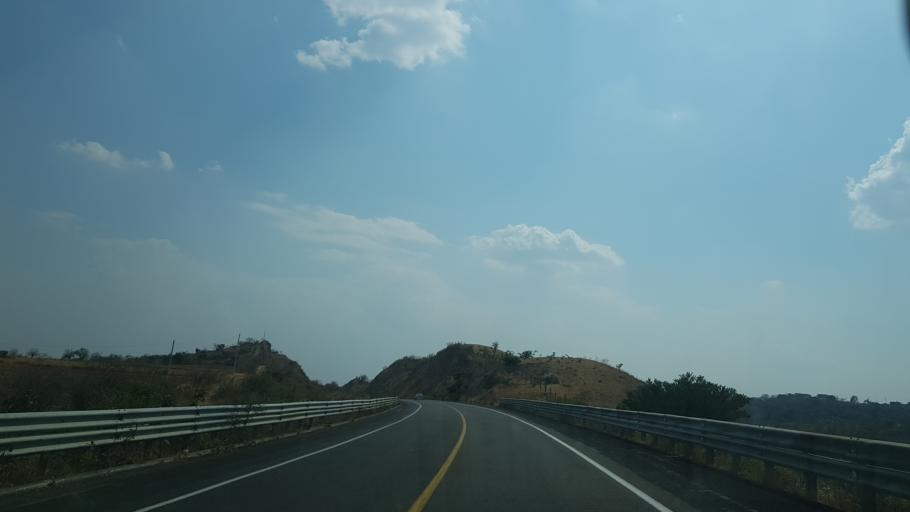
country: MX
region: Morelos
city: Tlacotepec
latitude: 18.8102
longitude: -98.7025
